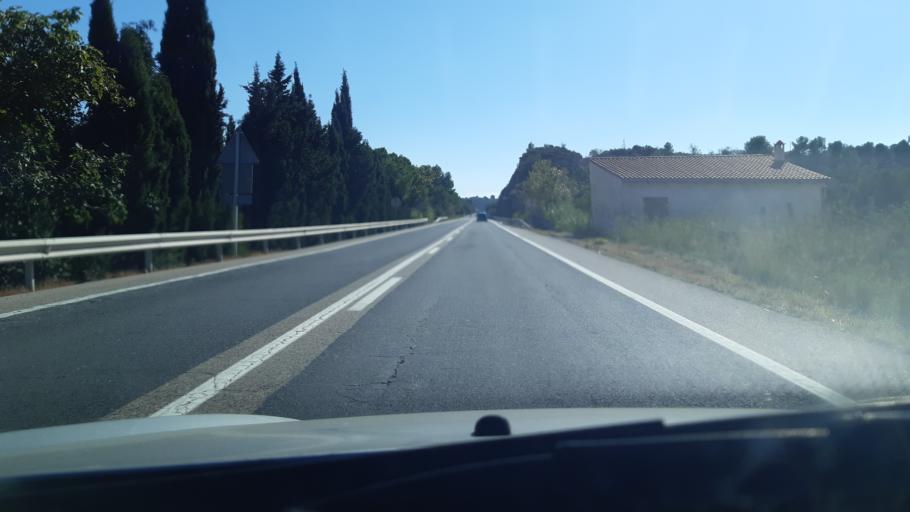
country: ES
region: Catalonia
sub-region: Provincia de Tarragona
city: Tivenys
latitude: 40.8952
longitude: 0.4886
